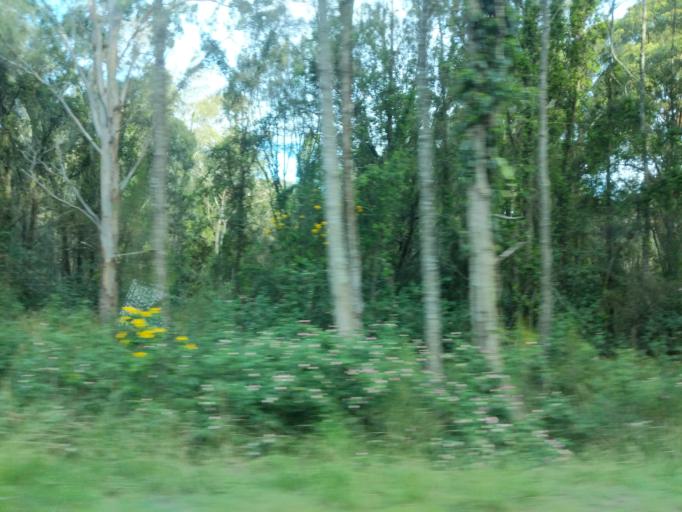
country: AU
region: New South Wales
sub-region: Port Stephens Shire
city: Port Stephens
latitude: -32.6659
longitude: 152.0161
